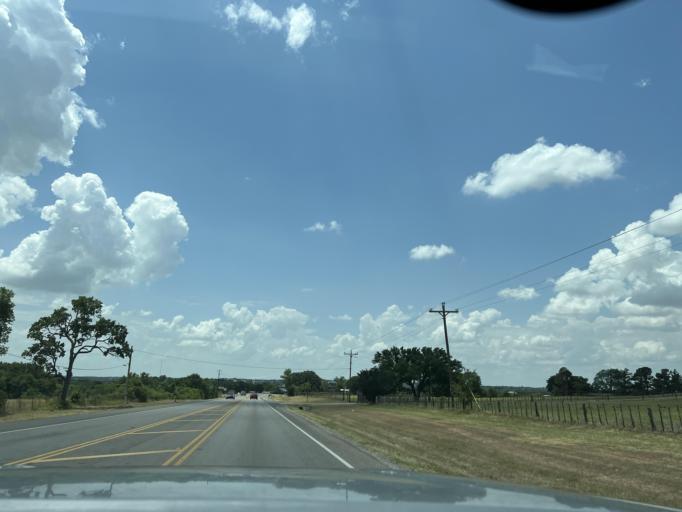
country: US
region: Texas
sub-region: Parker County
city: Weatherford
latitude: 32.8149
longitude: -97.7778
